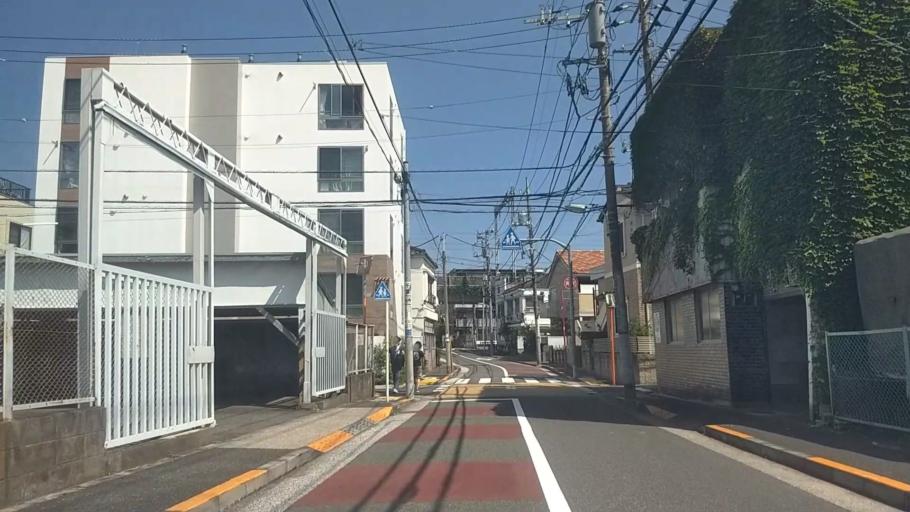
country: JP
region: Kanagawa
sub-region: Kawasaki-shi
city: Kawasaki
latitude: 35.6073
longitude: 139.7230
